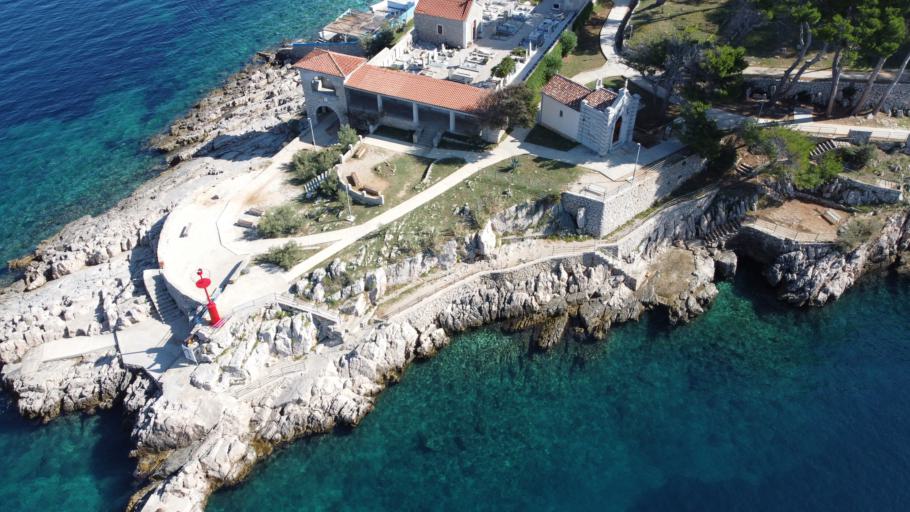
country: HR
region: Primorsko-Goranska
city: Mali Losinj
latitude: 44.5236
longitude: 14.5008
